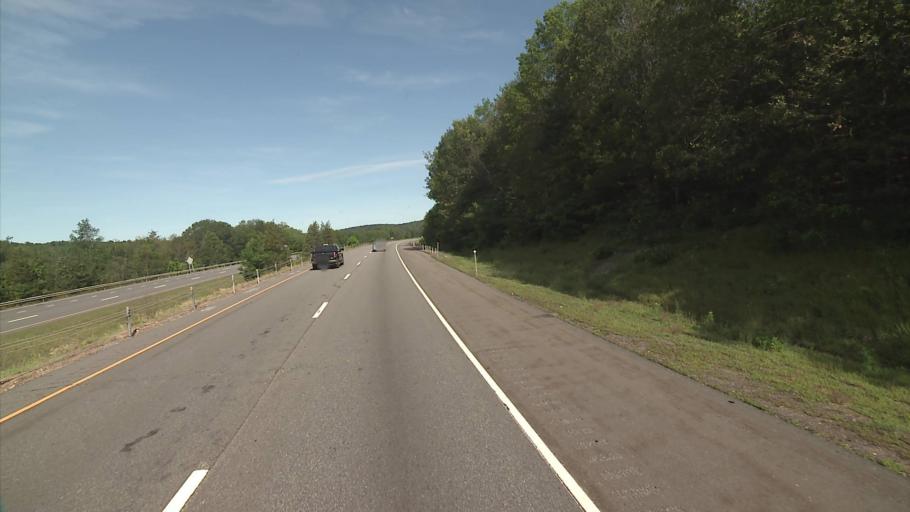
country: US
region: Connecticut
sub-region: New London County
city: Colchester
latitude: 41.5745
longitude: -72.3465
